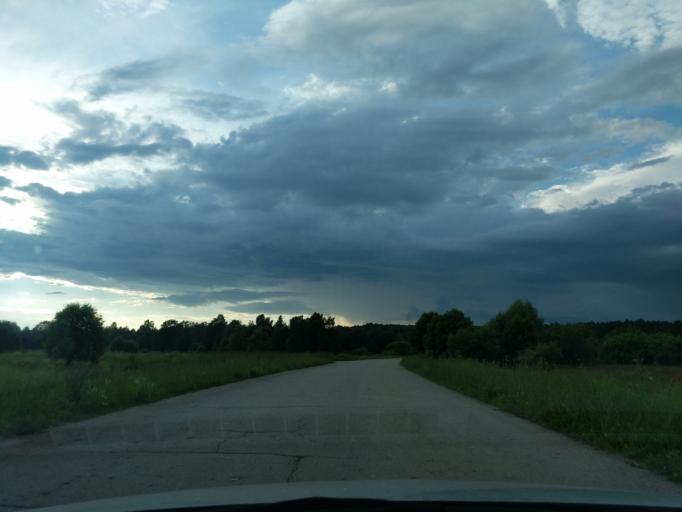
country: RU
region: Kaluga
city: Myatlevo
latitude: 54.8358
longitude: 35.6371
